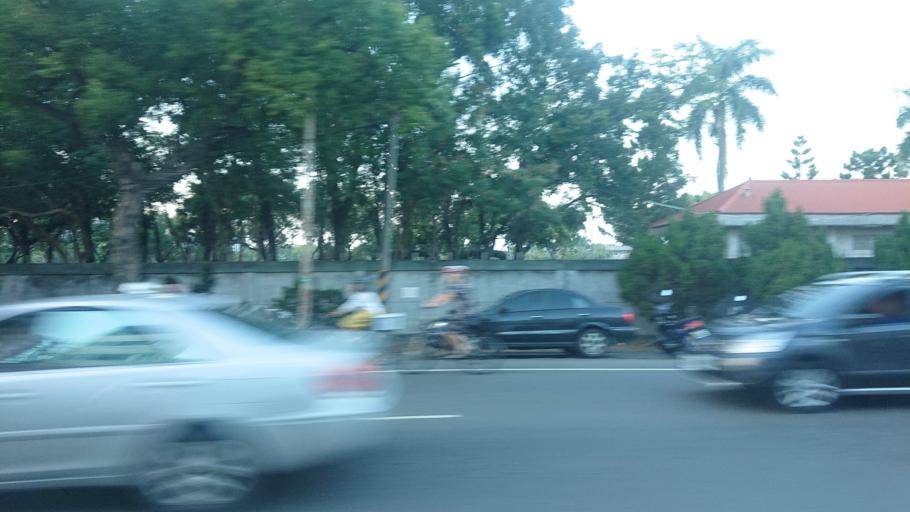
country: TW
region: Taiwan
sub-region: Tainan
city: Tainan
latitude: 23.0199
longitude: 120.2425
